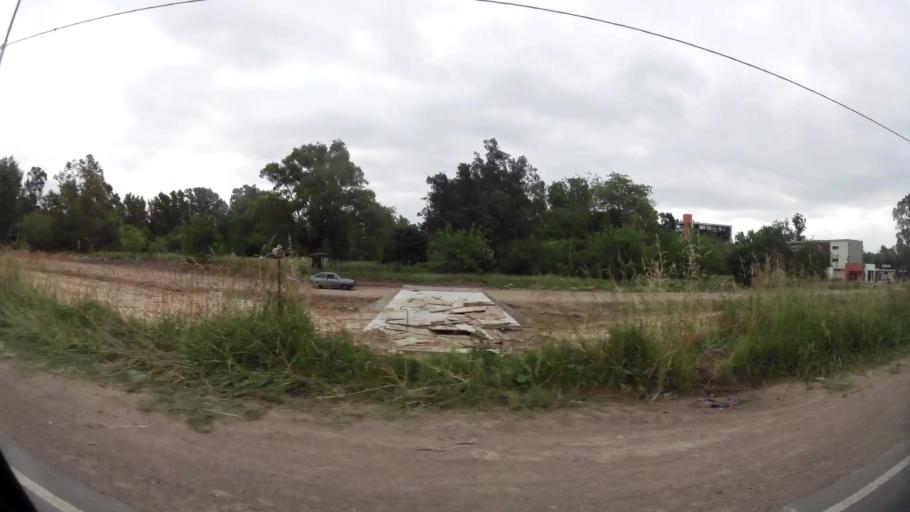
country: AR
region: Buenos Aires
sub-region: Partido de Ezeiza
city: Ezeiza
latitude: -34.8950
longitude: -58.5080
